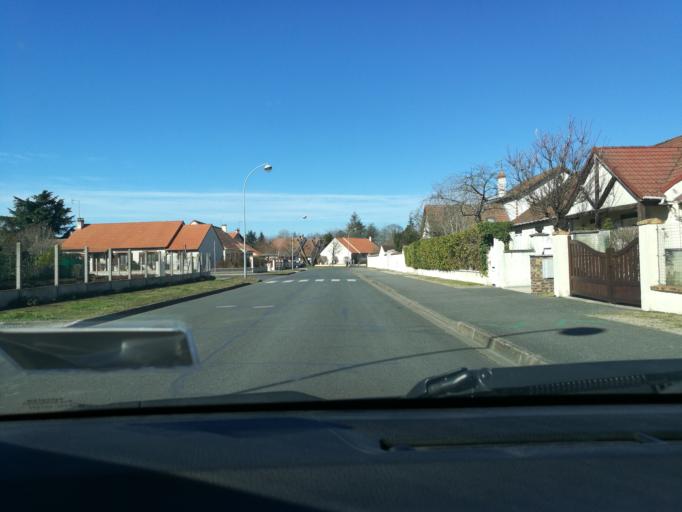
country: FR
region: Centre
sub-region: Departement du Loiret
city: Saint-Jean-le-Blanc
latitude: 47.8843
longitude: 1.9188
